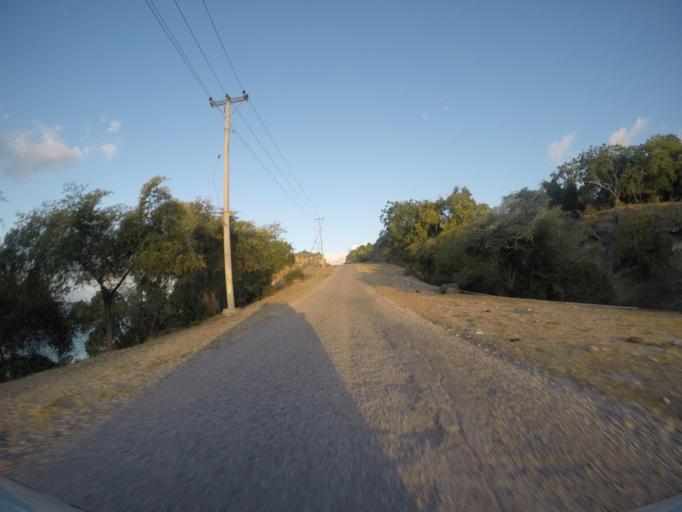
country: TL
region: Lautem
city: Lospalos
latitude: -8.3438
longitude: 127.0440
